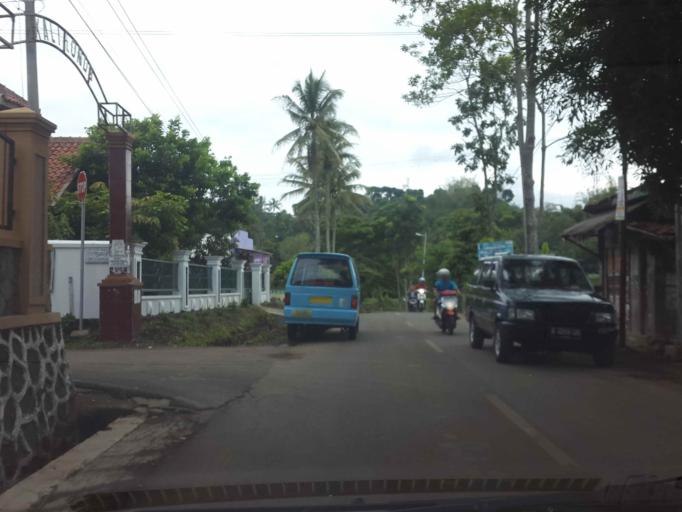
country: ID
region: Central Java
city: Salatiga
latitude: -7.3434
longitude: 110.5275
